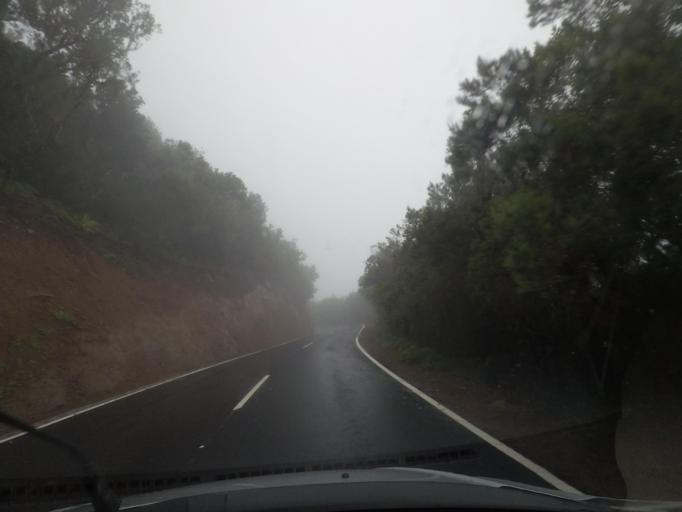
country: PT
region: Madeira
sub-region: Santana
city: Santana
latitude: 32.7716
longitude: -16.9088
